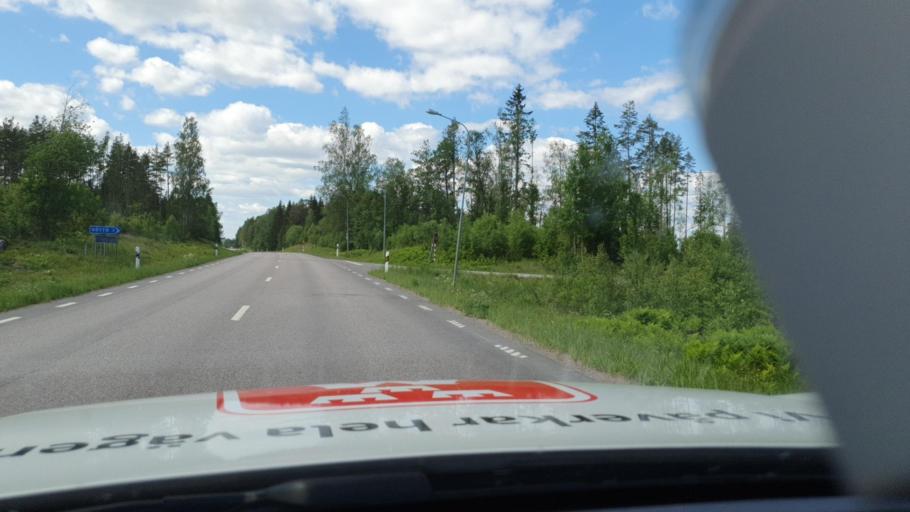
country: SE
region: Uppsala
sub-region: Tierps Kommun
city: Karlholmsbruk
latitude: 60.5331
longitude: 17.5827
